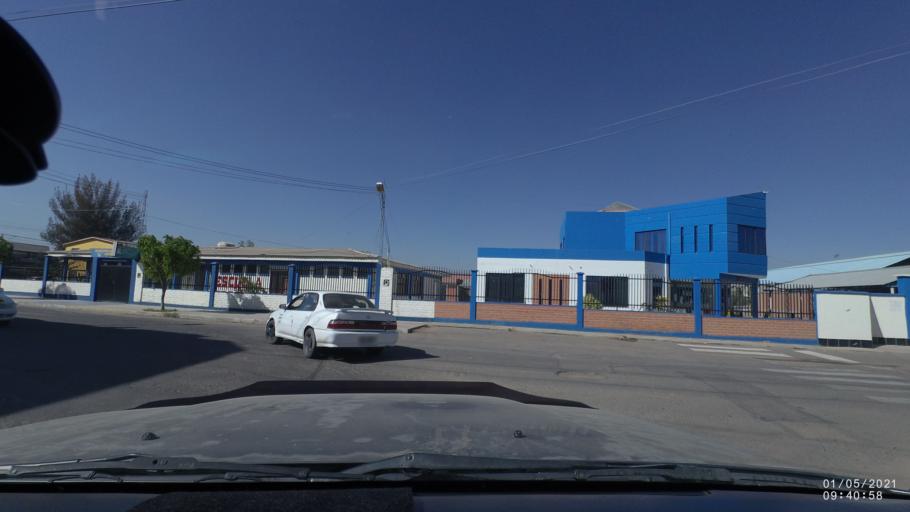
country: BO
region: Cochabamba
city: Cochabamba
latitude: -17.4203
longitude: -66.1676
